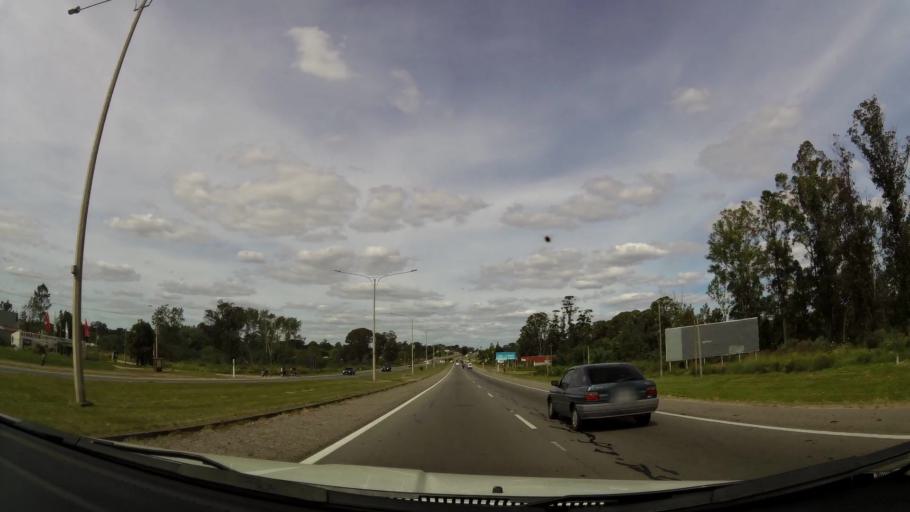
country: UY
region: Canelones
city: Empalme Olmos
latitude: -34.7807
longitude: -55.8735
